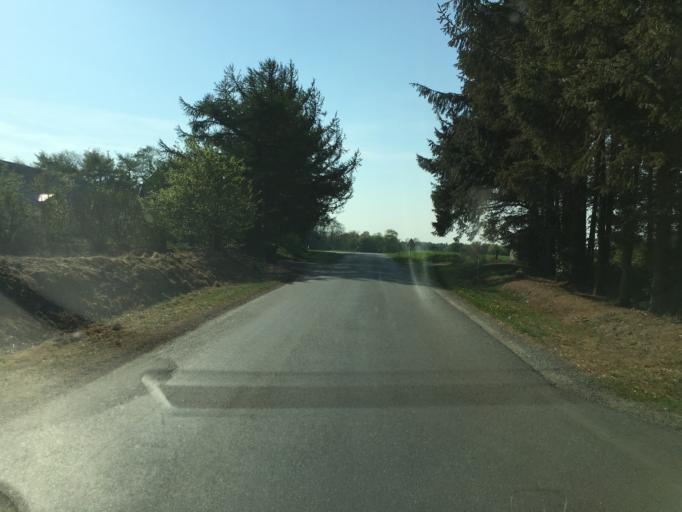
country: DK
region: South Denmark
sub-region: Haderslev Kommune
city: Vojens
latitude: 55.2329
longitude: 9.3335
